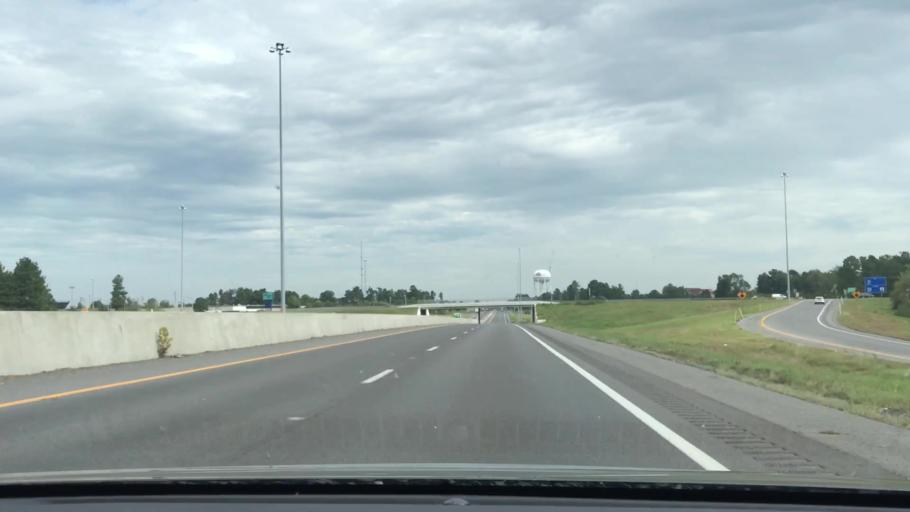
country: US
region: Kentucky
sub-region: Graves County
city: Mayfield
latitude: 36.7550
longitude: -88.6591
